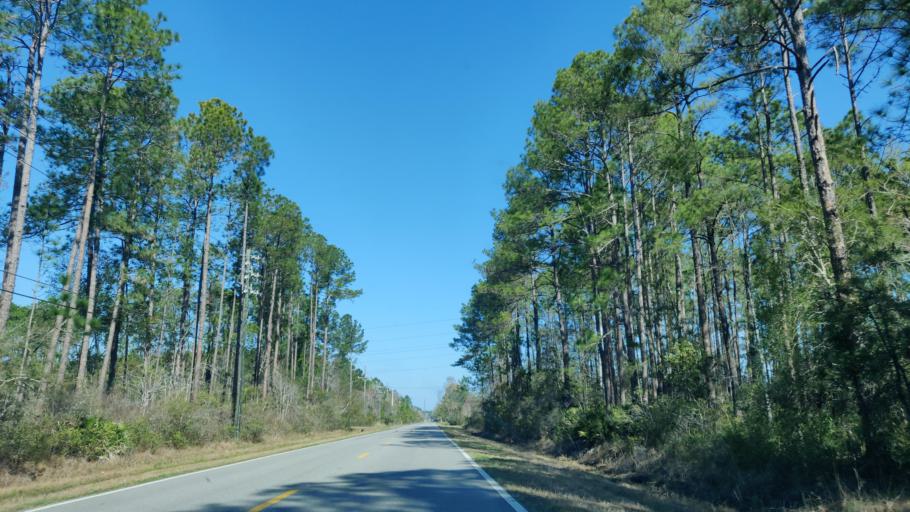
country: US
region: Florida
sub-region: Duval County
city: Baldwin
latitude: 30.2730
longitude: -81.9596
